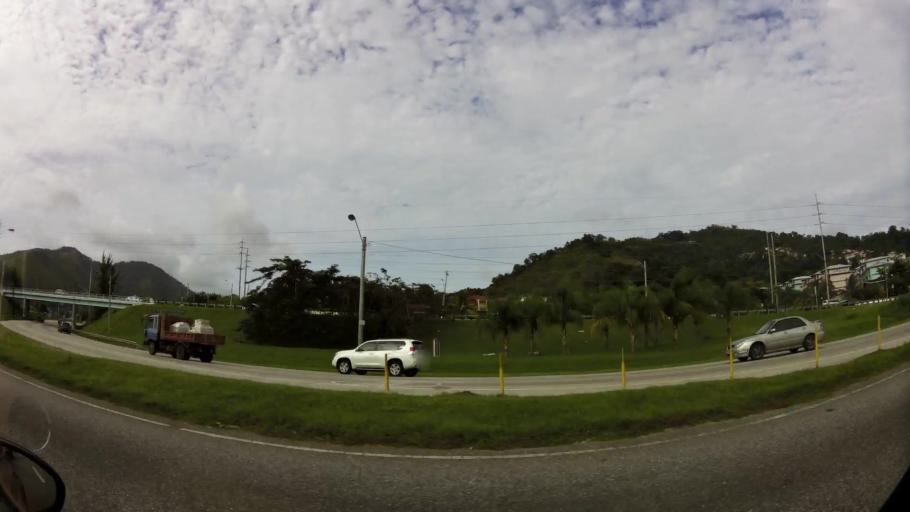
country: TT
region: City of Port of Spain
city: Mucurapo
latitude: 10.6786
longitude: -61.5515
